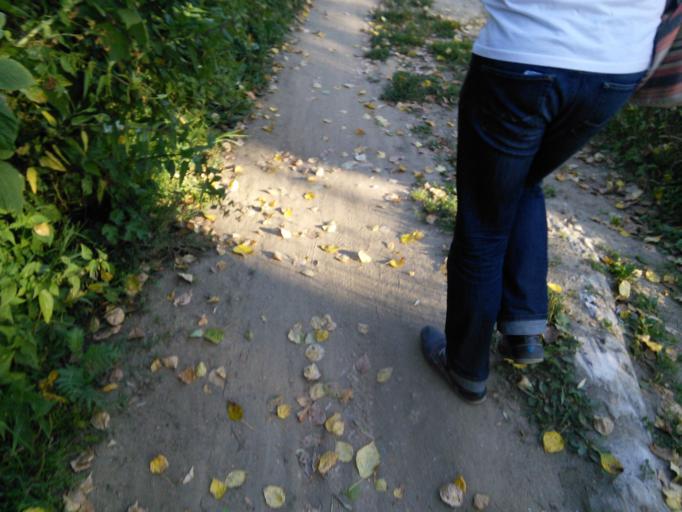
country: RU
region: Moskovskaya
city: Pavlovskiy Posad
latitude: 55.7877
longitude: 38.6819
